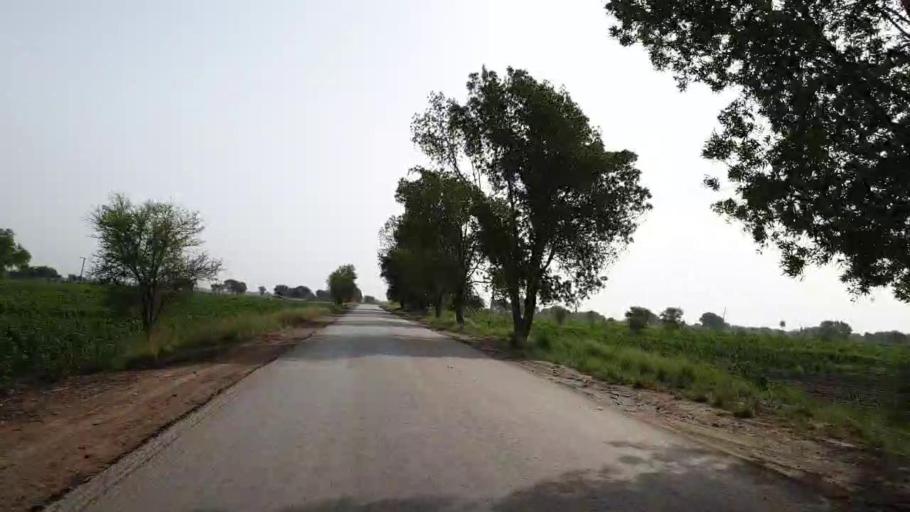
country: PK
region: Sindh
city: Nawabshah
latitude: 26.2544
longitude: 68.4659
